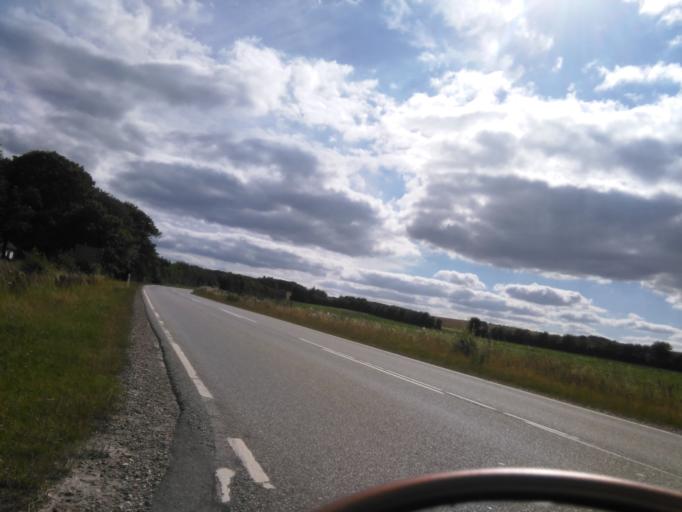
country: DK
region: Central Jutland
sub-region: Skanderborg Kommune
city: Skovby
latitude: 56.1153
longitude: 9.9861
